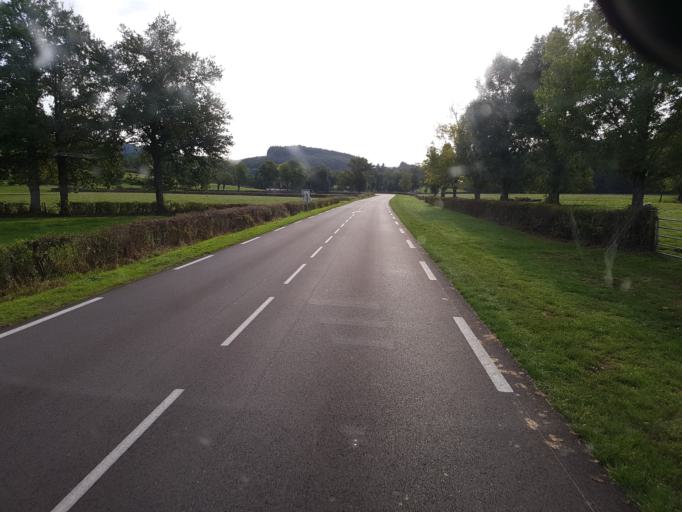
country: FR
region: Bourgogne
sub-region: Departement de Saone-et-Loire
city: La Clayette
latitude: 46.2815
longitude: 4.3602
